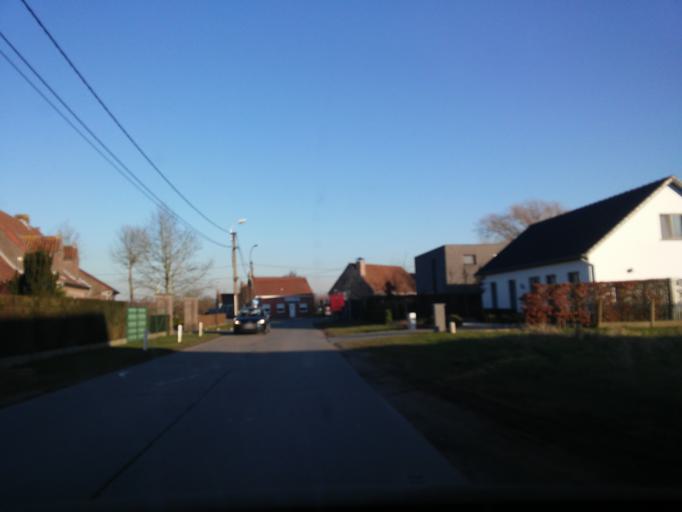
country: BE
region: Flanders
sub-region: Provincie Oost-Vlaanderen
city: Eeklo
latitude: 51.1756
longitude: 3.5050
